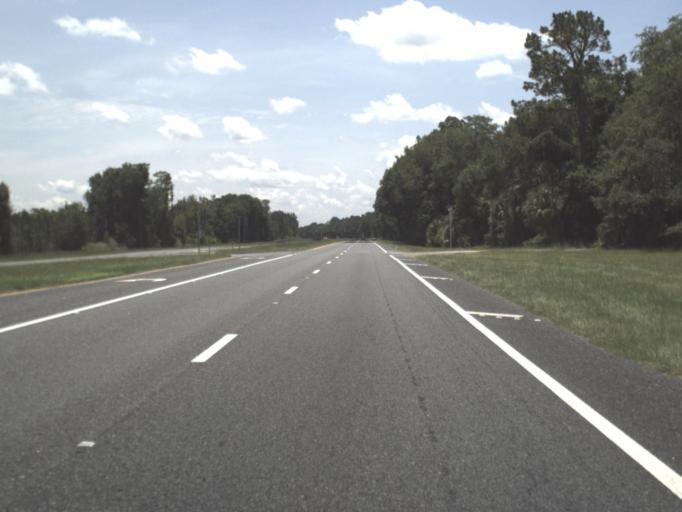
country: US
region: Florida
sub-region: Taylor County
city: Steinhatchee
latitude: 29.7388
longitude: -83.3175
